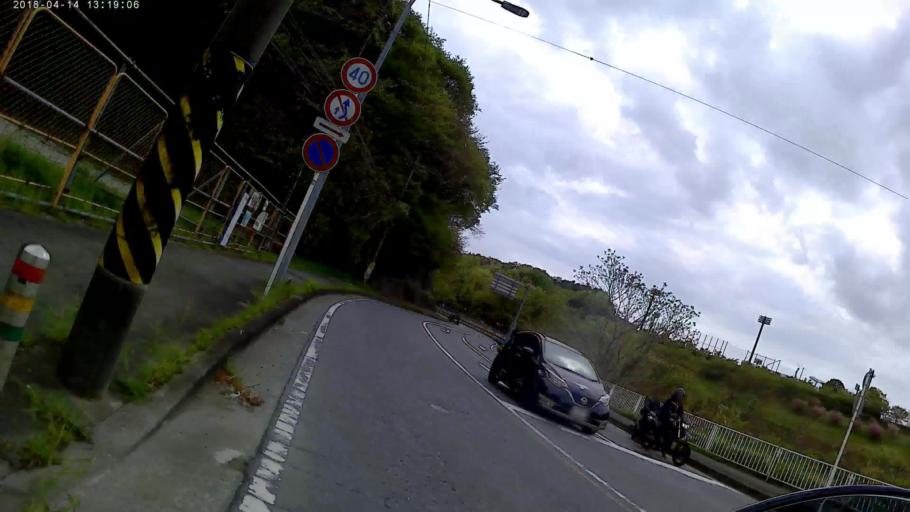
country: JP
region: Kanagawa
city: Hadano
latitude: 35.3413
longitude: 139.2221
